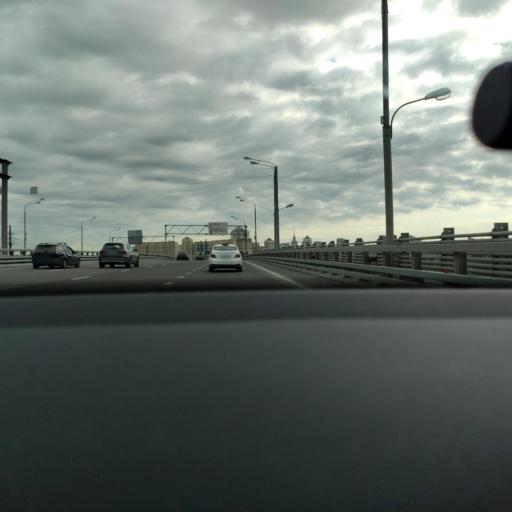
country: RU
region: Moscow
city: Amin'yevo
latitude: 55.6995
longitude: 37.4706
